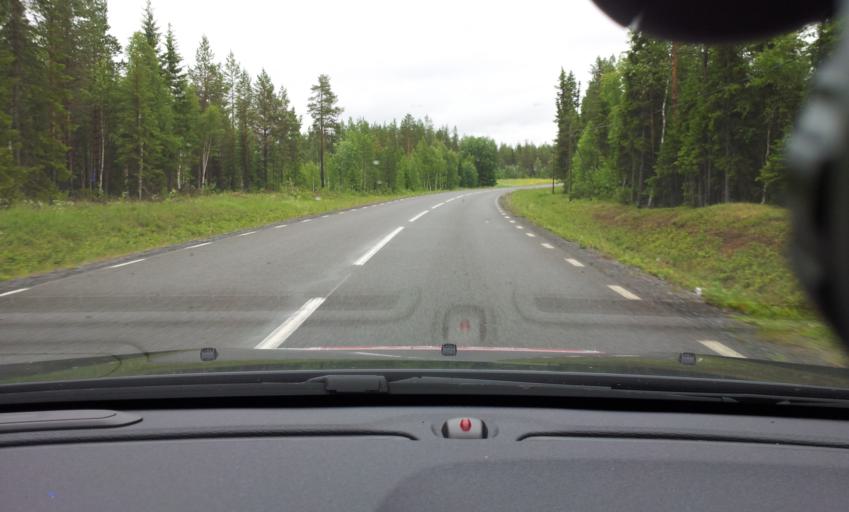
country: SE
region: Jaemtland
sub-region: OEstersunds Kommun
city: Lit
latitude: 63.6927
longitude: 15.0068
